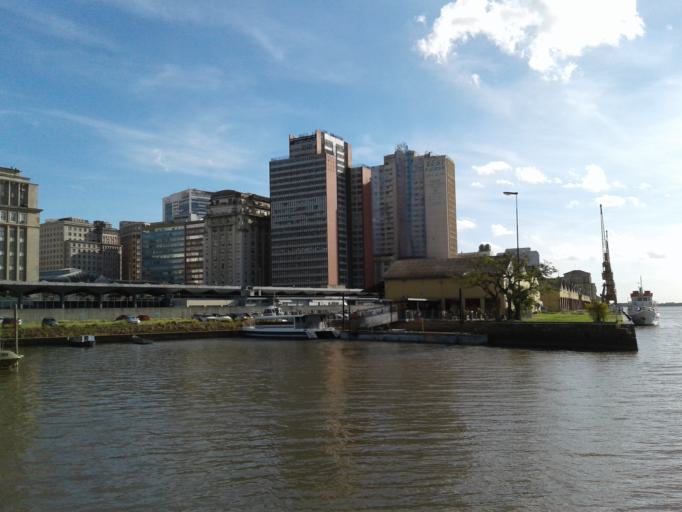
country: BR
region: Rio Grande do Sul
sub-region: Porto Alegre
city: Porto Alegre
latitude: -30.0249
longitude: -51.2272
